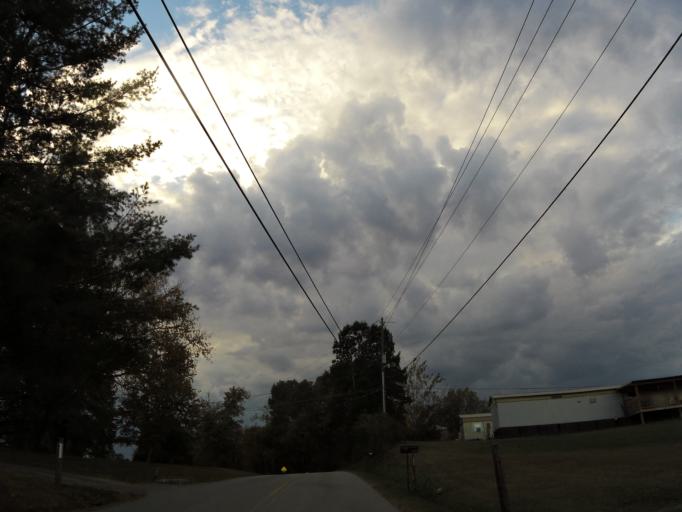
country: US
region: Tennessee
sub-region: Blount County
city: Louisville
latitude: 35.7687
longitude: -84.0429
